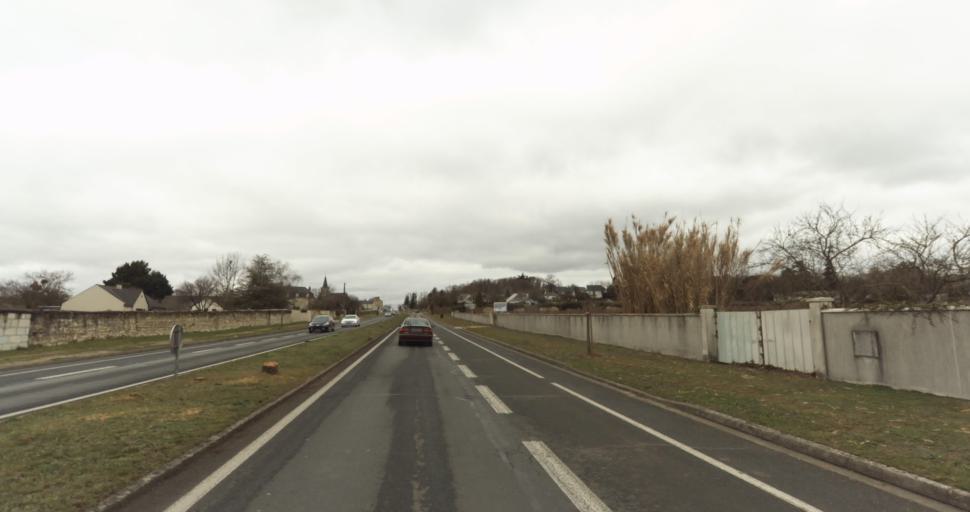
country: FR
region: Pays de la Loire
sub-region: Departement de Maine-et-Loire
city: Varrains
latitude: 47.2238
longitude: -0.0630
